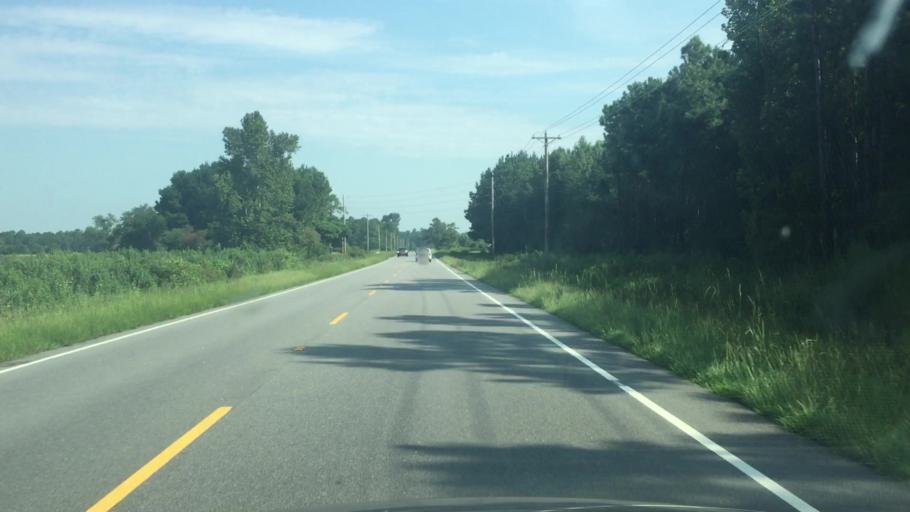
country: US
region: North Carolina
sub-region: Columbus County
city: Tabor City
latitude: 34.2236
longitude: -78.8241
